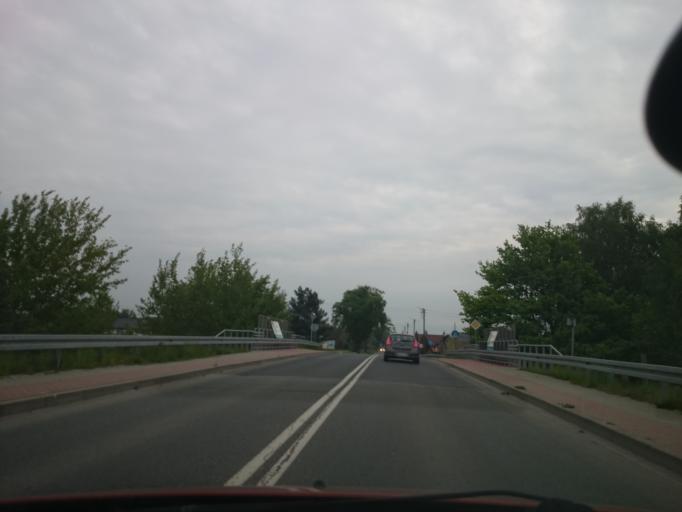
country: PL
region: Opole Voivodeship
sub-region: Powiat opolski
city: Dobrzen Wielki
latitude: 50.7750
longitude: 17.8568
